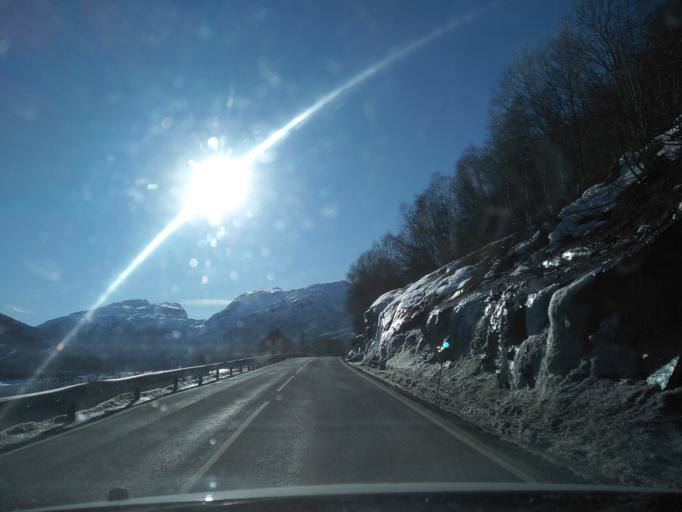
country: NO
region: Hordaland
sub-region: Odda
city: Odda
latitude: 59.8302
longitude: 6.8084
